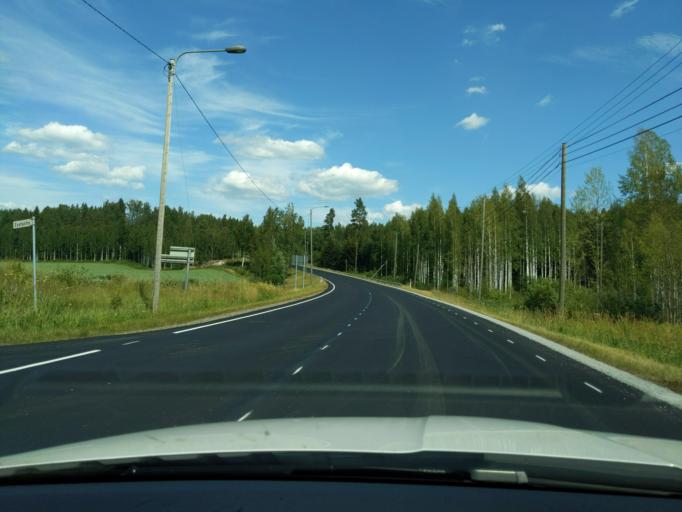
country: FI
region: Paijanne Tavastia
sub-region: Lahti
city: Nastola
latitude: 61.0749
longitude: 25.8273
